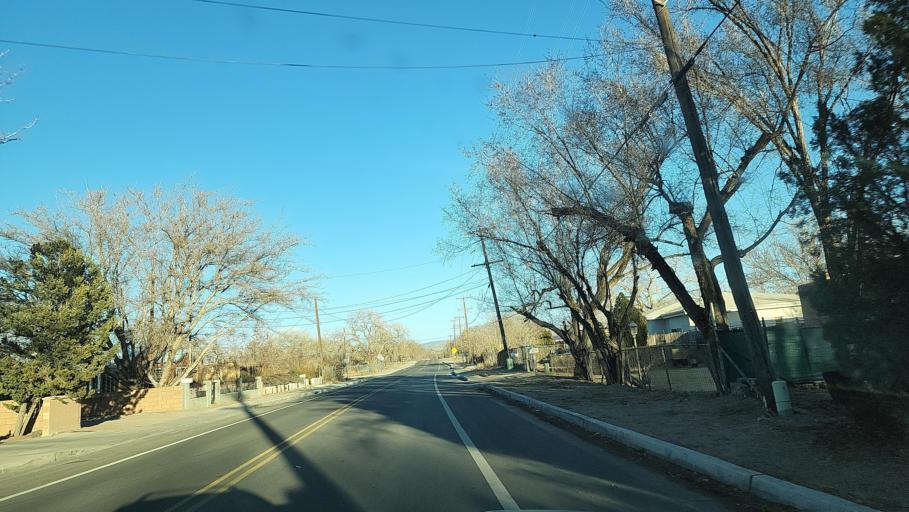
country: US
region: New Mexico
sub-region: Bernalillo County
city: South Valley
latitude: 35.0307
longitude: -106.6873
